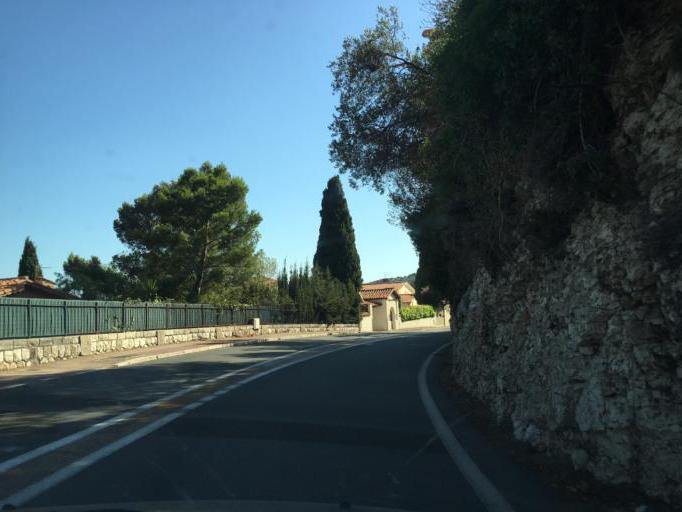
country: FR
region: Provence-Alpes-Cote d'Azur
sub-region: Departement des Alpes-Maritimes
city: Villefranche-sur-Mer
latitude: 43.7092
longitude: 7.3088
